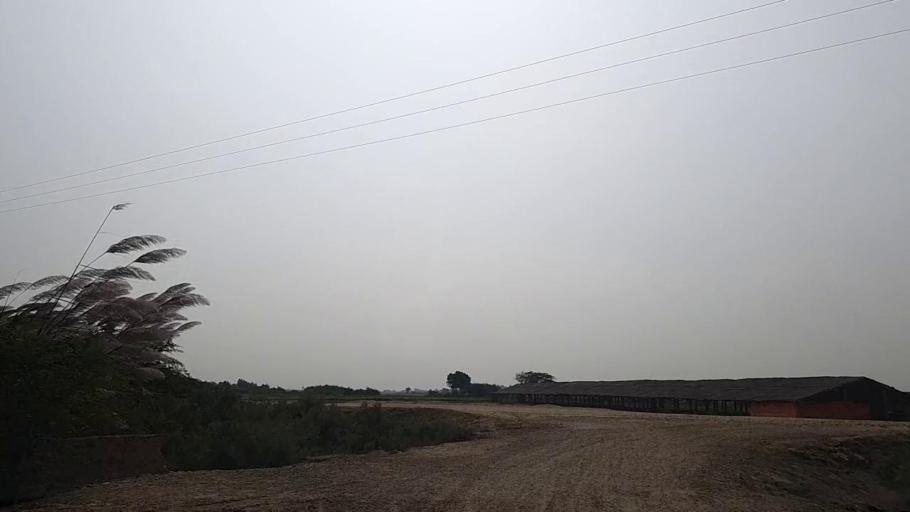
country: PK
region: Sindh
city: Mirpur Sakro
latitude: 24.6294
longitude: 67.7680
